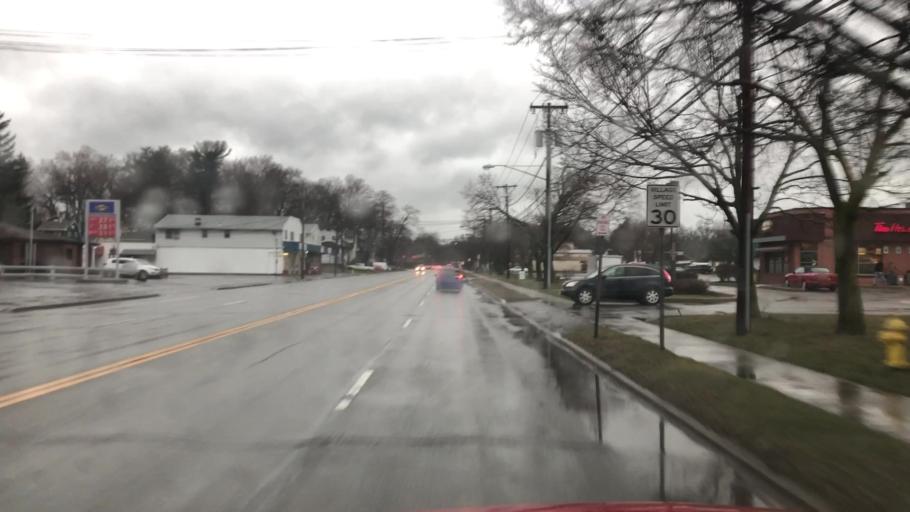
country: US
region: New York
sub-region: Monroe County
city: East Rochester
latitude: 43.1157
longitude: -77.4949
